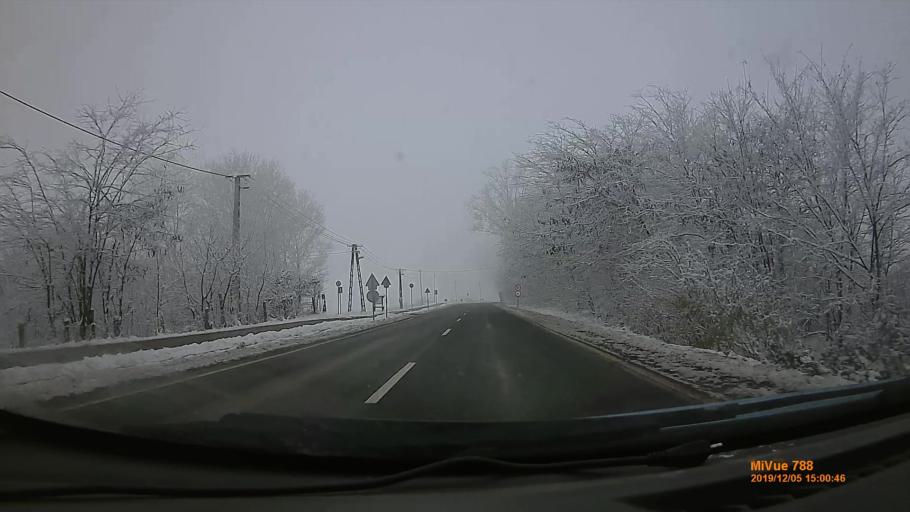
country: HU
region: Szabolcs-Szatmar-Bereg
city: Tiszanagyfalu
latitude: 48.0655
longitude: 21.5361
